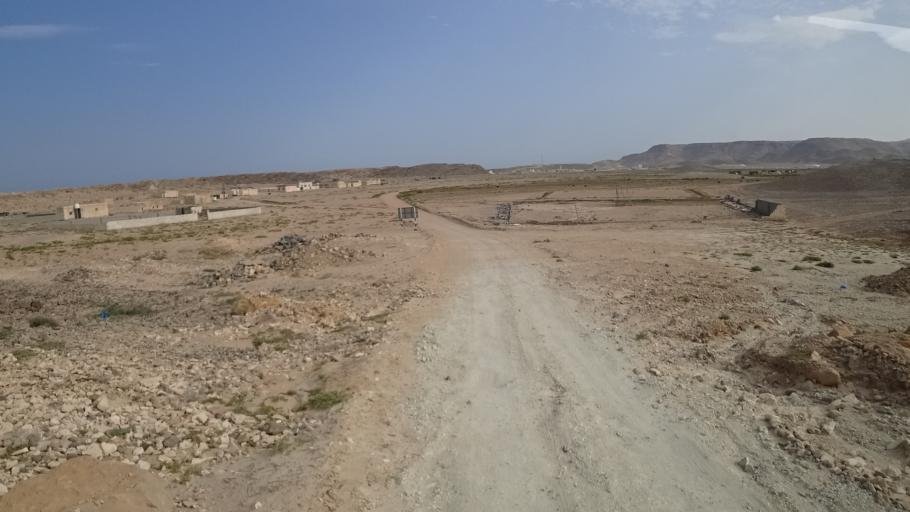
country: OM
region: Ash Sharqiyah
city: Sur
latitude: 22.4513
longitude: 59.8252
